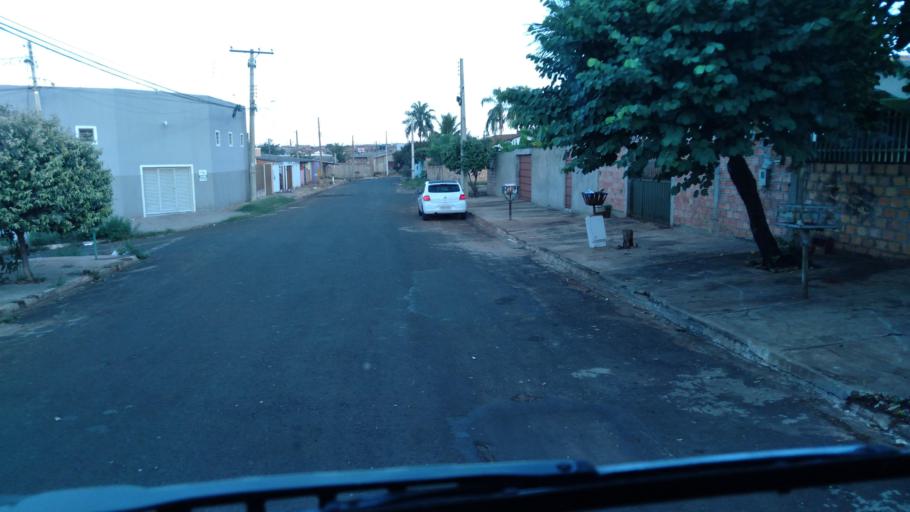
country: BR
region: Goias
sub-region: Mineiros
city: Mineiros
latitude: -17.5732
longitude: -52.5694
